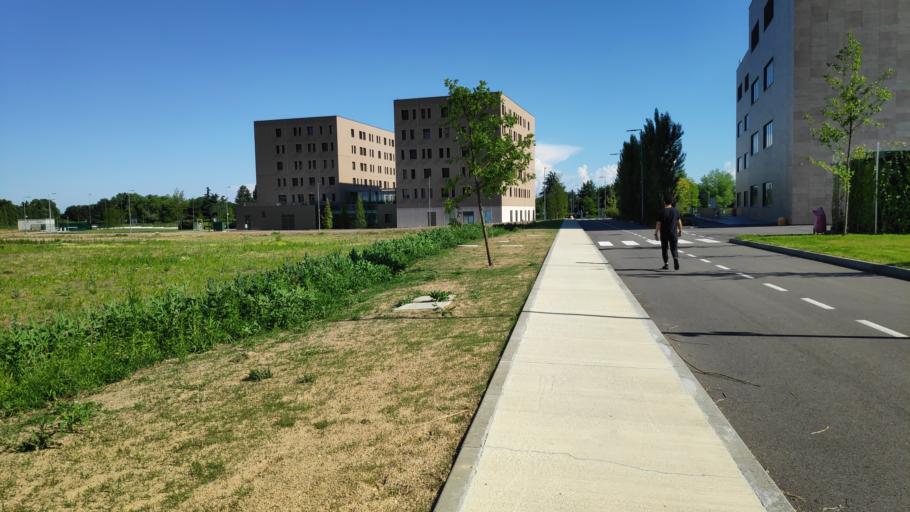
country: IT
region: Lombardy
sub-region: Citta metropolitana di Milano
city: Basiglio
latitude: 45.3708
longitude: 9.1720
